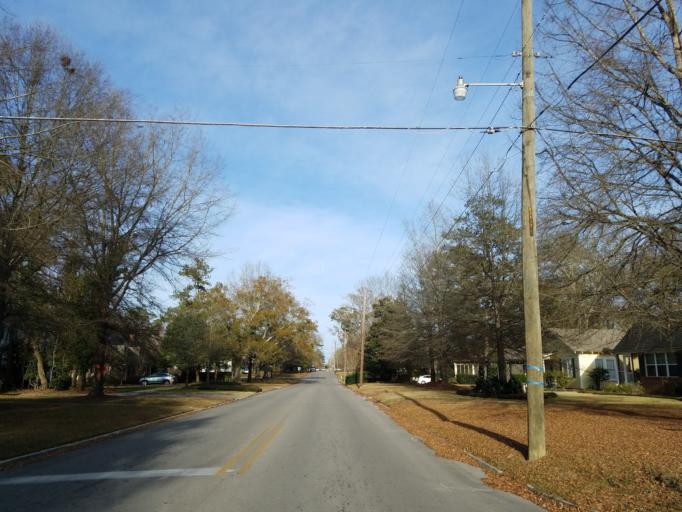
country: US
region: Mississippi
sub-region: Forrest County
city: Hattiesburg
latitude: 31.3190
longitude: -89.3039
